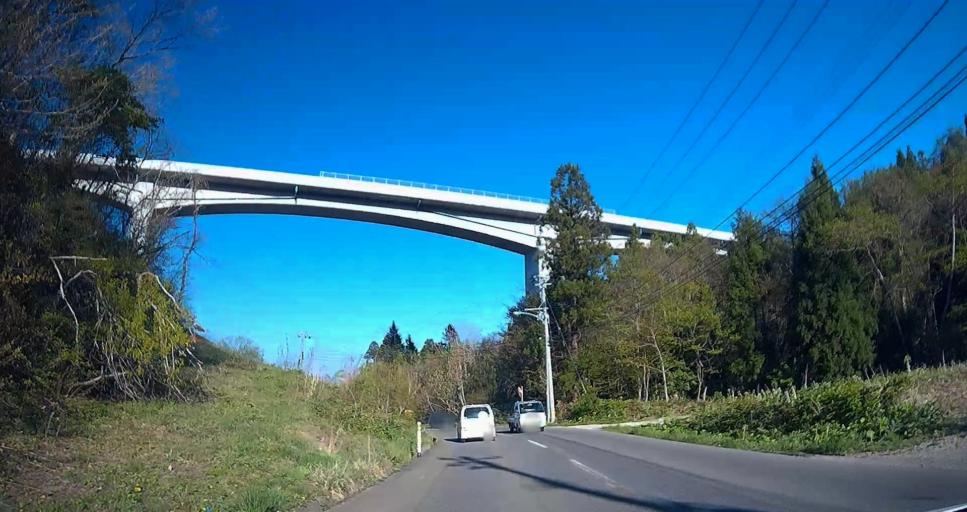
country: JP
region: Aomori
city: Mutsu
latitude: 41.4217
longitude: 141.1479
